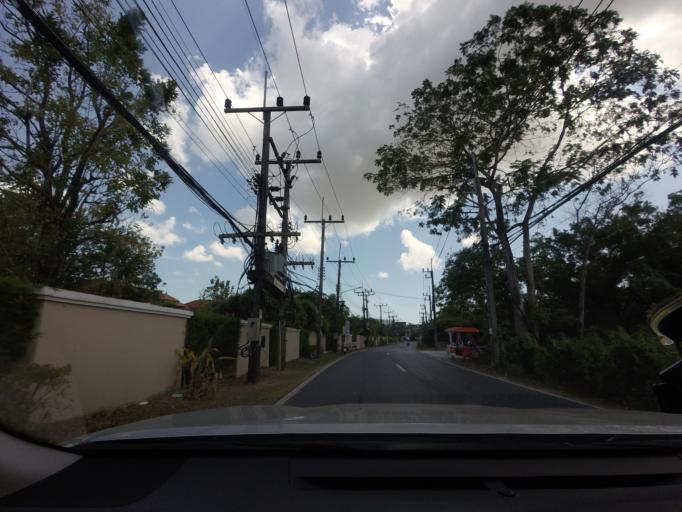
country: TH
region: Phuket
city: Thalang
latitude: 8.0190
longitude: 98.3036
